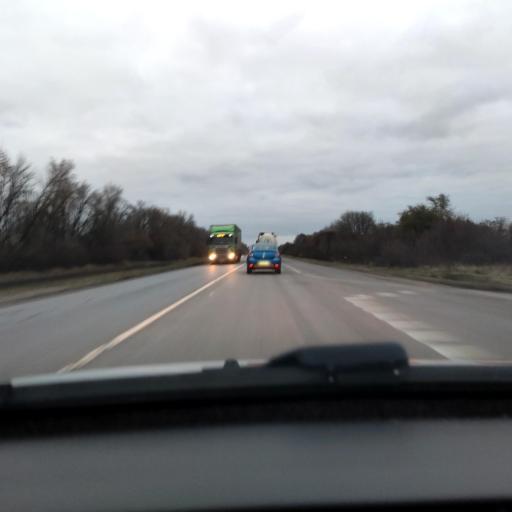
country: RU
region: Lipetsk
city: Borinskoye
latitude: 52.4484
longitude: 39.2920
